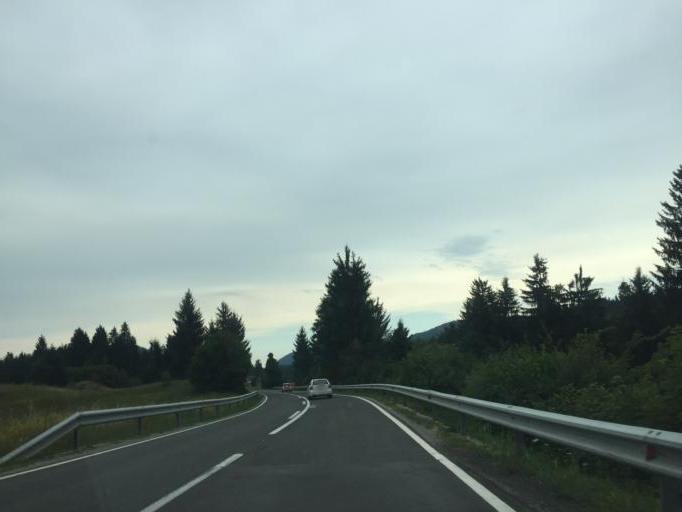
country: SI
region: Logatec
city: Logatec
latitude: 45.8980
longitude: 14.1847
